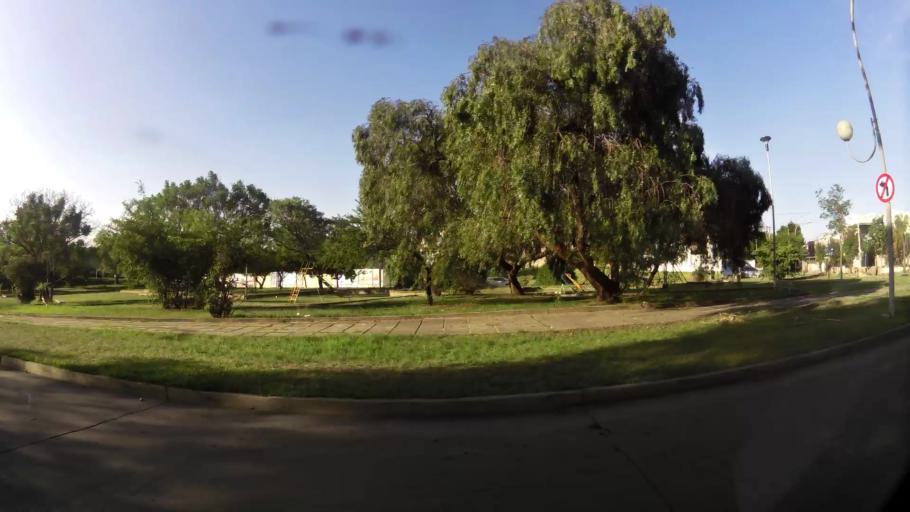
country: AR
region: Cordoba
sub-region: Departamento de Capital
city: Cordoba
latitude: -31.3838
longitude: -64.2459
